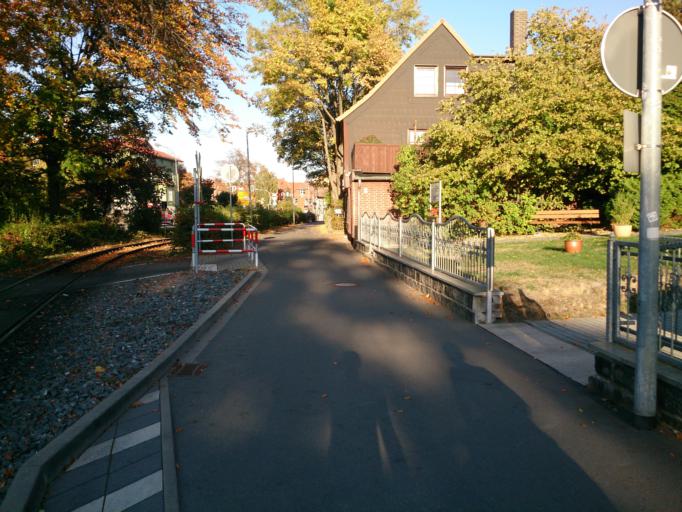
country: DE
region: Saxony-Anhalt
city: Wernigerode
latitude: 51.8315
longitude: 10.7790
